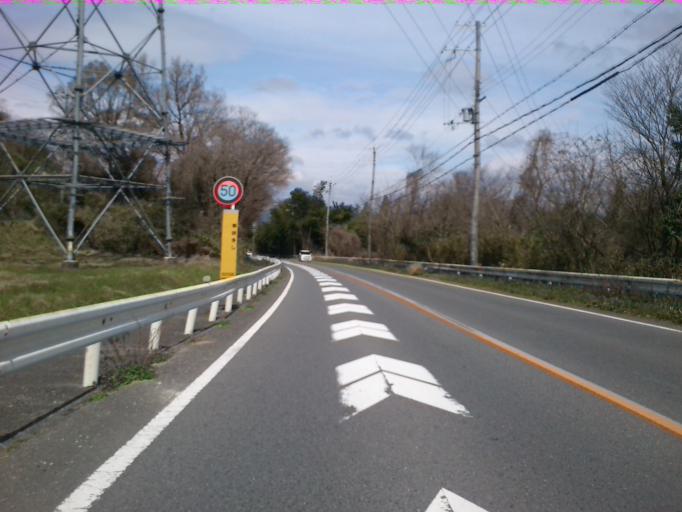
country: JP
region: Nara
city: Nara-shi
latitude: 34.7272
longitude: 135.8575
